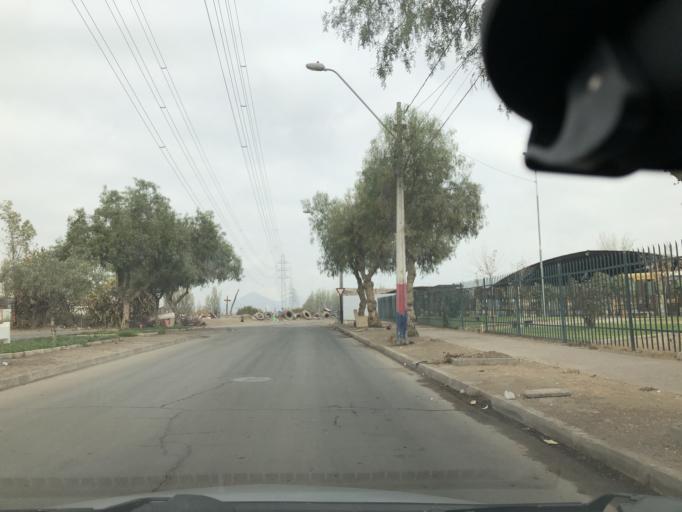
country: CL
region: Santiago Metropolitan
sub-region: Provincia de Cordillera
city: Puente Alto
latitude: -33.5967
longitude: -70.6026
